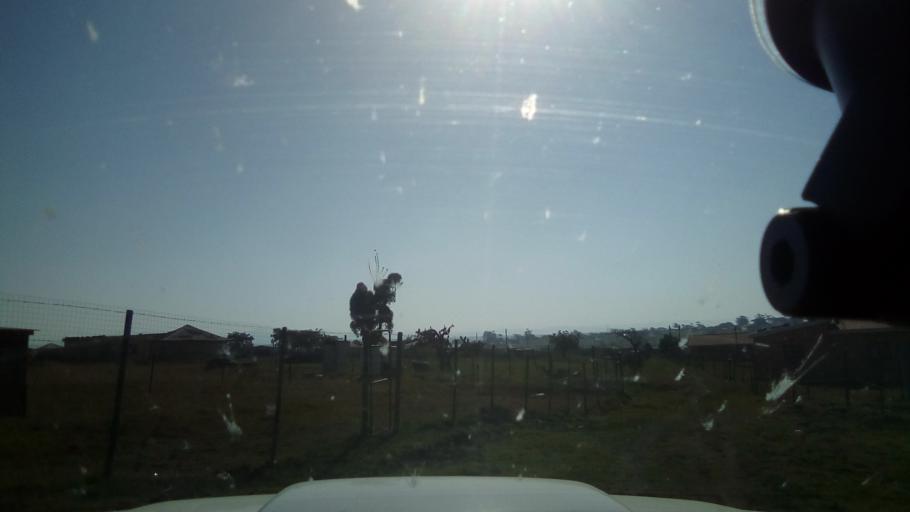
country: ZA
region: Eastern Cape
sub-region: Buffalo City Metropolitan Municipality
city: Bhisho
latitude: -32.9511
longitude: 27.3235
